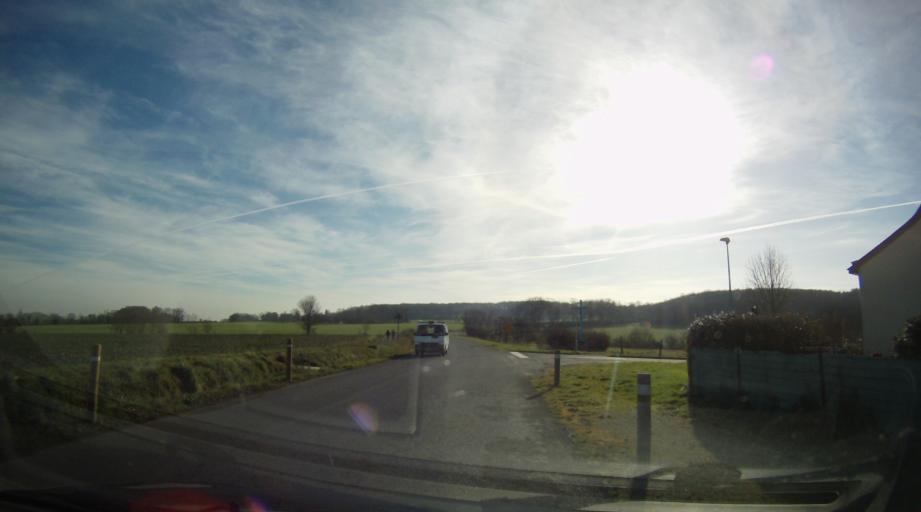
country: FR
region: Brittany
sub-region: Departement d'Ille-et-Vilaine
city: Orgeres
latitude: 47.9926
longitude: -1.6637
